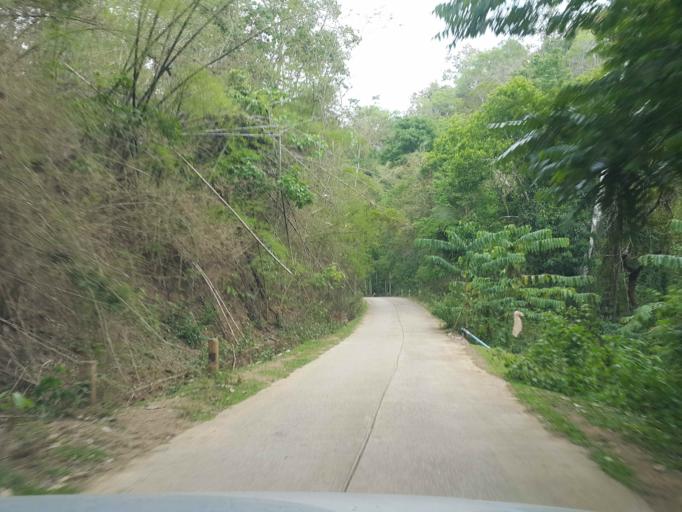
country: TH
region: Chiang Mai
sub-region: Amphoe Chiang Dao
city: Chiang Dao
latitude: 19.3755
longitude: 98.7530
